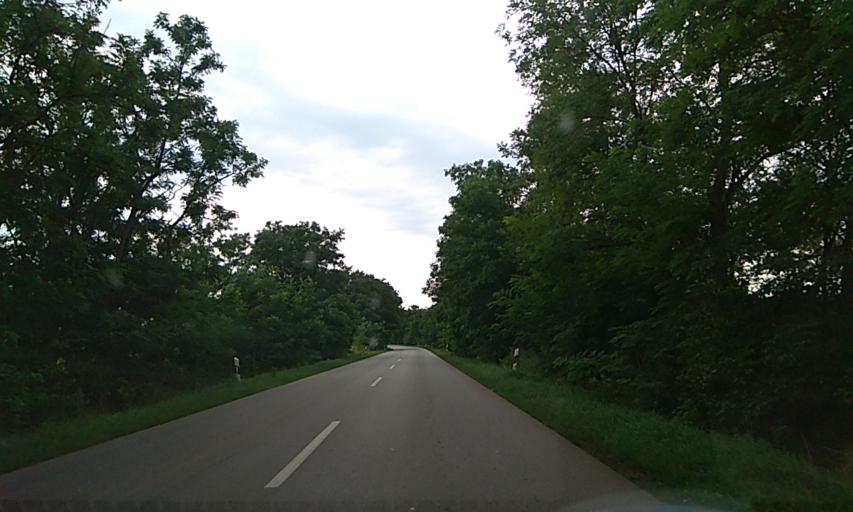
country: HU
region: Szabolcs-Szatmar-Bereg
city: Buj
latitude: 48.0866
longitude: 21.6406
